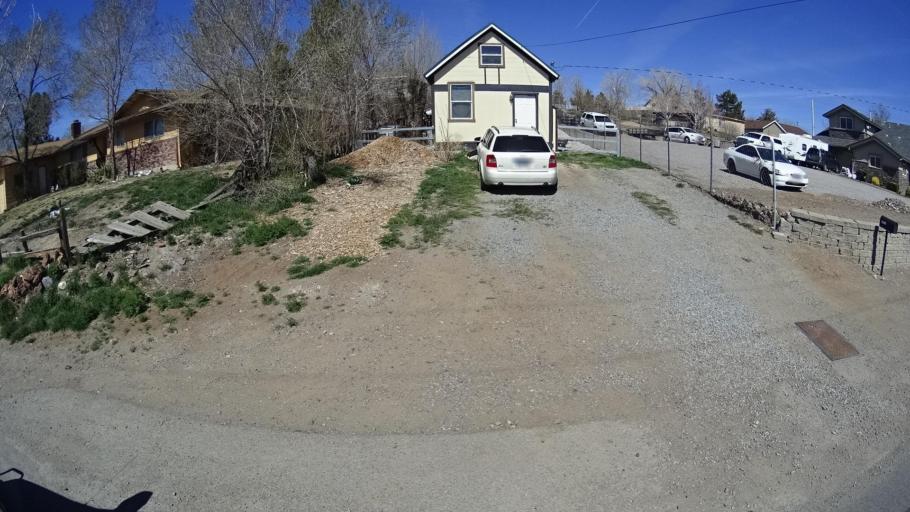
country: US
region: Nevada
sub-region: Washoe County
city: Sparks
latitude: 39.5540
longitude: -119.7724
